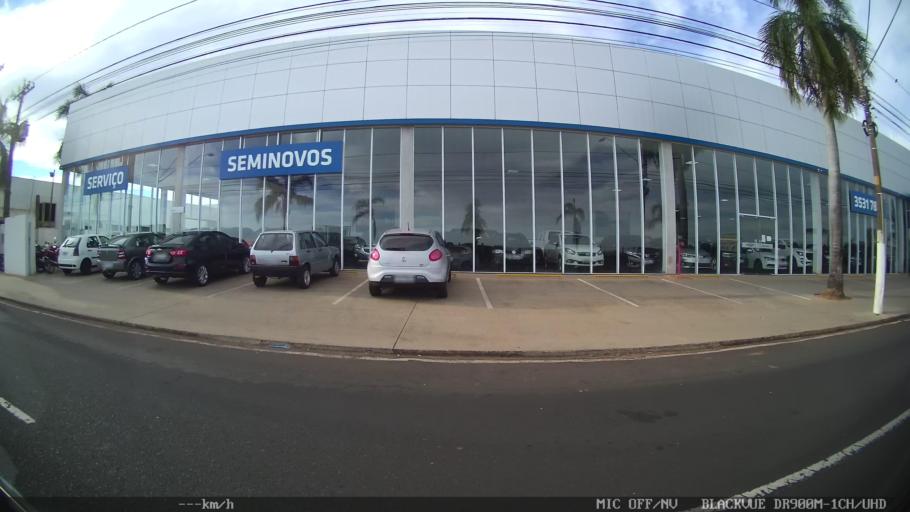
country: BR
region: Sao Paulo
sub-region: Catanduva
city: Catanduva
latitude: -21.1509
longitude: -48.9894
